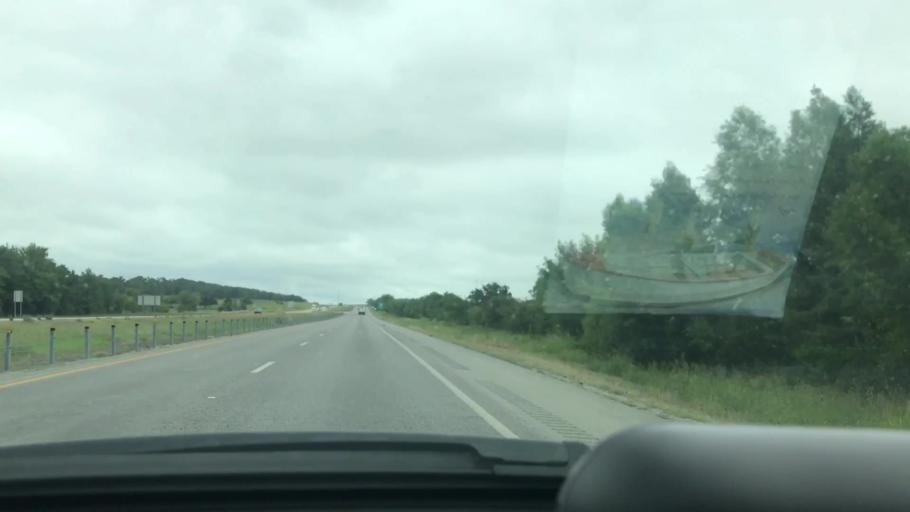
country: US
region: Oklahoma
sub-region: Coal County
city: Coalgate
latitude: 34.6617
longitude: -95.9392
